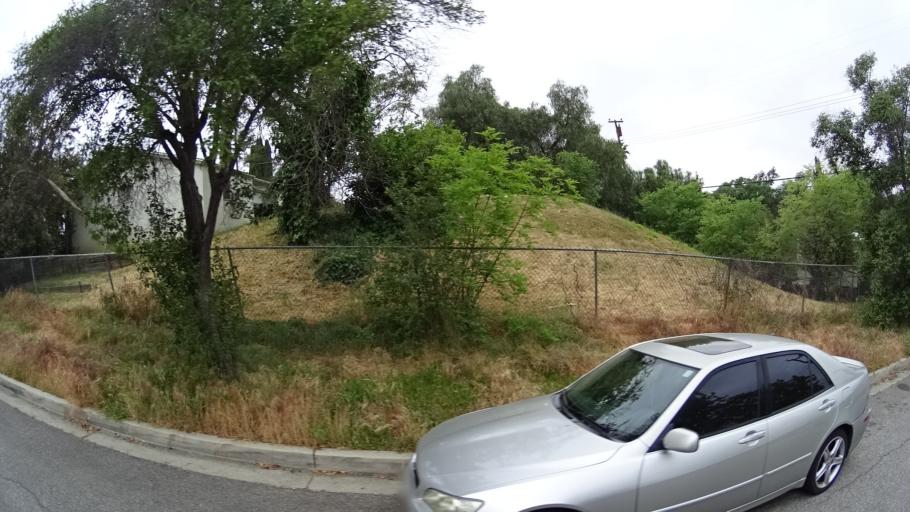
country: US
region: California
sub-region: Ventura County
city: Thousand Oaks
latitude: 34.2088
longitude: -118.8594
